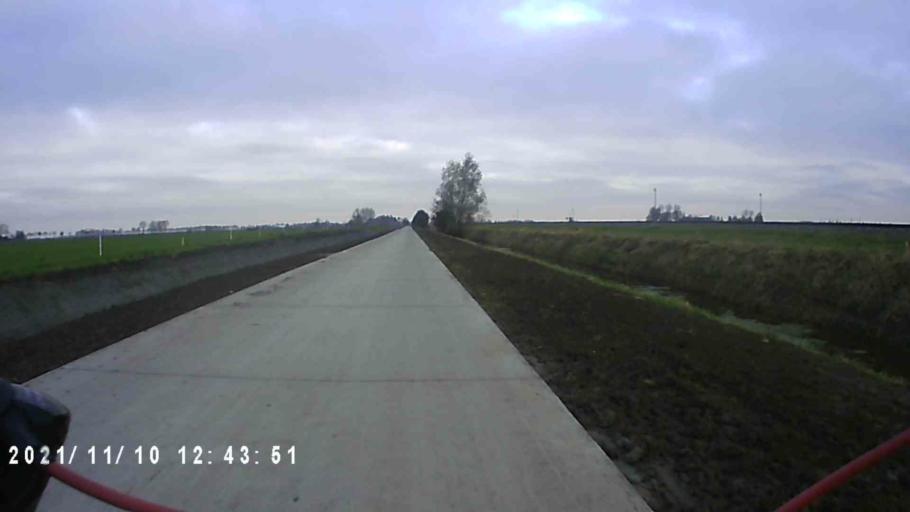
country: NL
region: Groningen
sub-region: Gemeente Groningen
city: Korrewegwijk
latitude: 53.2551
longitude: 6.5506
